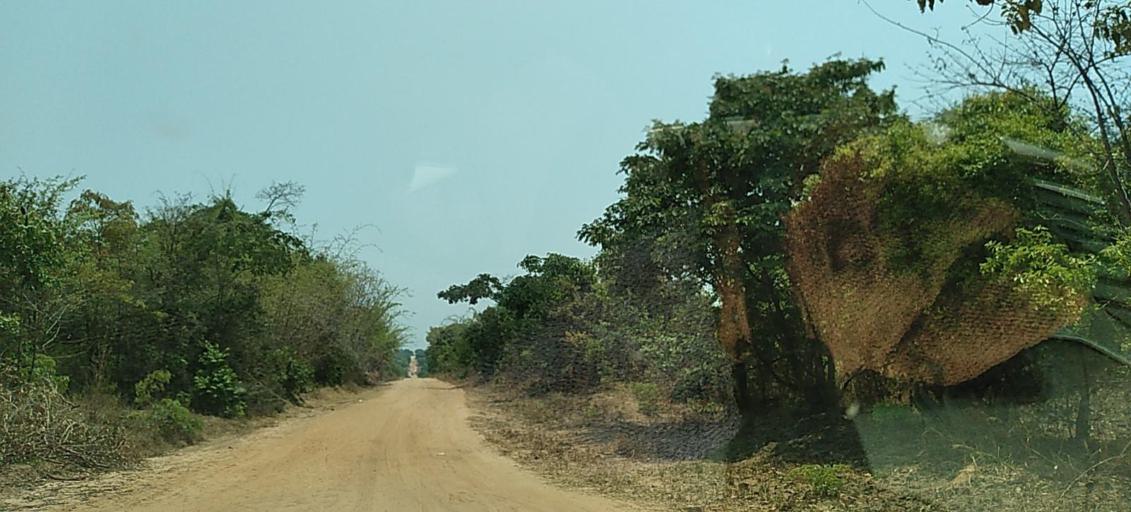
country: ZM
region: Copperbelt
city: Kalulushi
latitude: -12.9374
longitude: 28.1614
